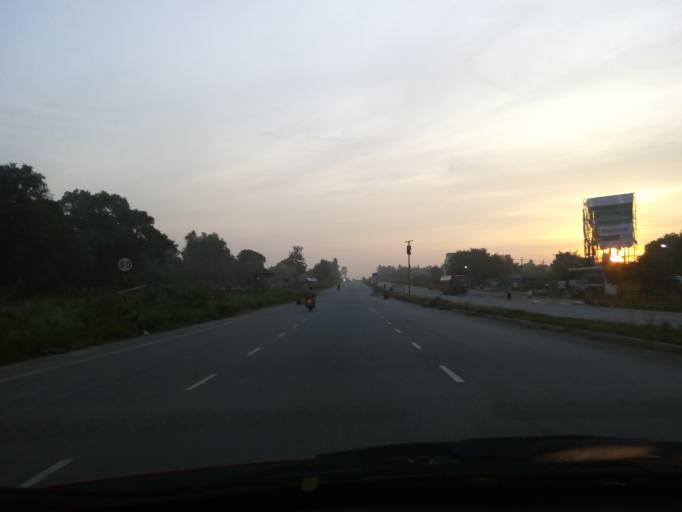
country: IN
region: Karnataka
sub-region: Bangalore Rural
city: Devanhalli
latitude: 13.2207
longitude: 77.6816
